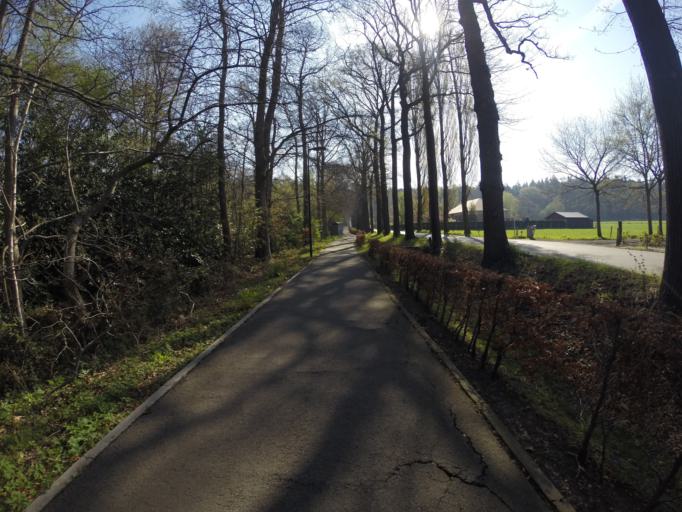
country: BE
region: Flanders
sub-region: Provincie Oost-Vlaanderen
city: Knesselare
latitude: 51.0947
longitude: 3.3817
